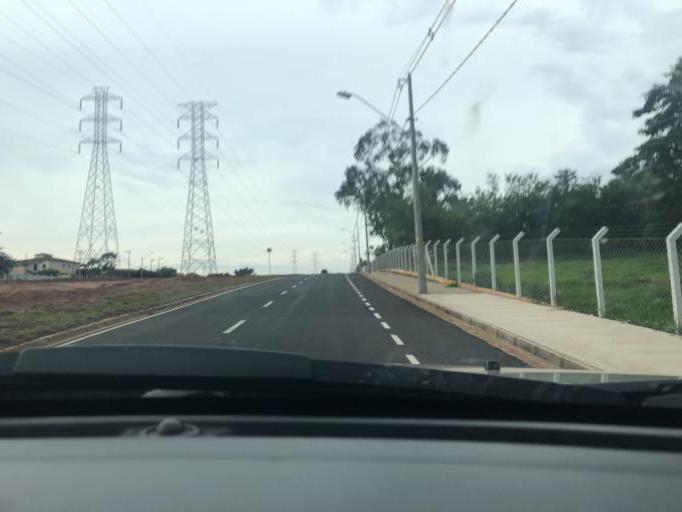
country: BR
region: Sao Paulo
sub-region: Sao Jose Do Rio Preto
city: Sao Jose do Rio Preto
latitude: -20.8432
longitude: -49.4096
